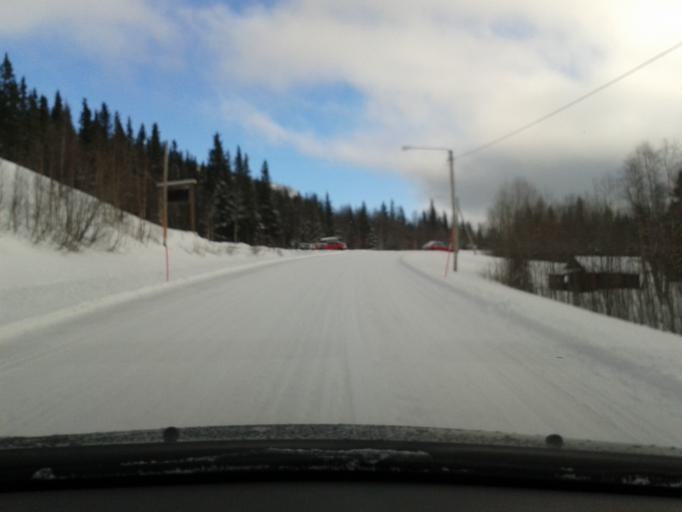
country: SE
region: Vaesterbotten
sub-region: Vilhelmina Kommun
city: Sjoberg
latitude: 65.2523
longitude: 15.5535
